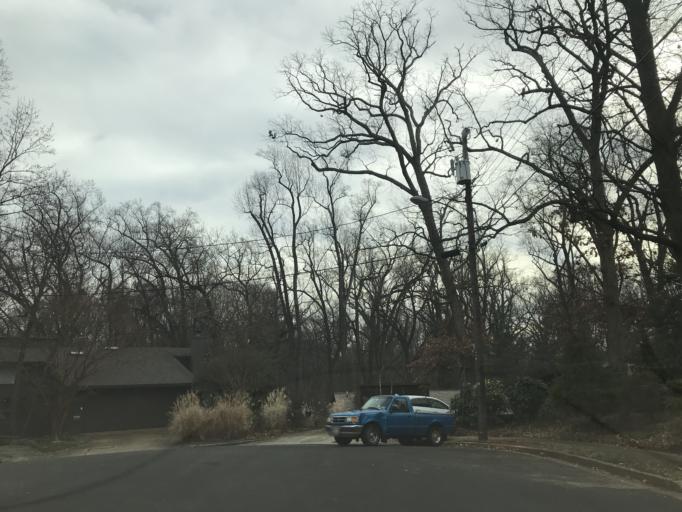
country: US
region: Virginia
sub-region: Arlington County
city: Arlington
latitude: 38.9031
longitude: -77.0946
